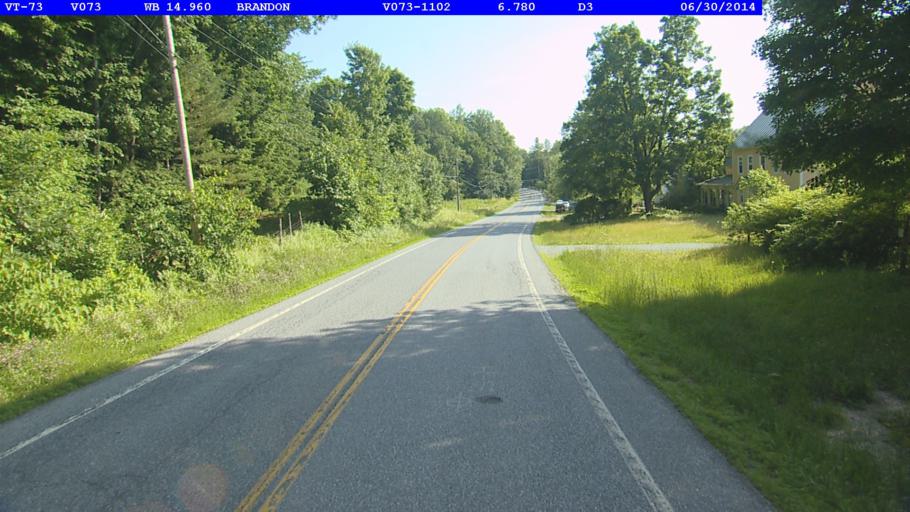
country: US
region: Vermont
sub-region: Rutland County
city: Brandon
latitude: 43.8364
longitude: -73.0413
